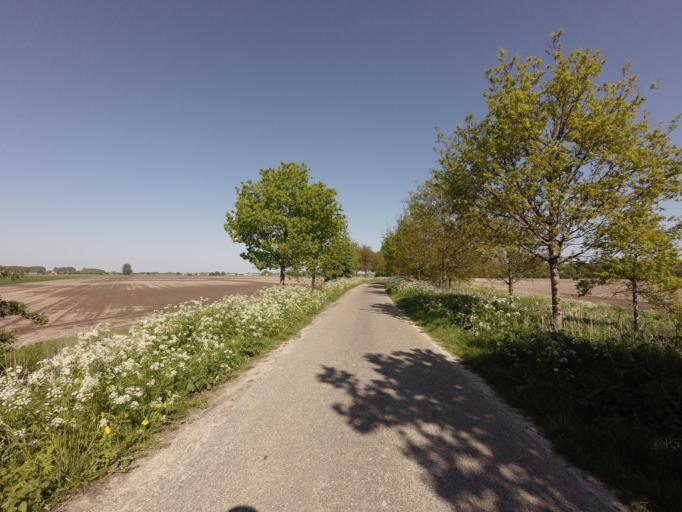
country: NL
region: North Brabant
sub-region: Gemeente Moerdijk
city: Klundert
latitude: 51.6312
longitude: 4.6089
